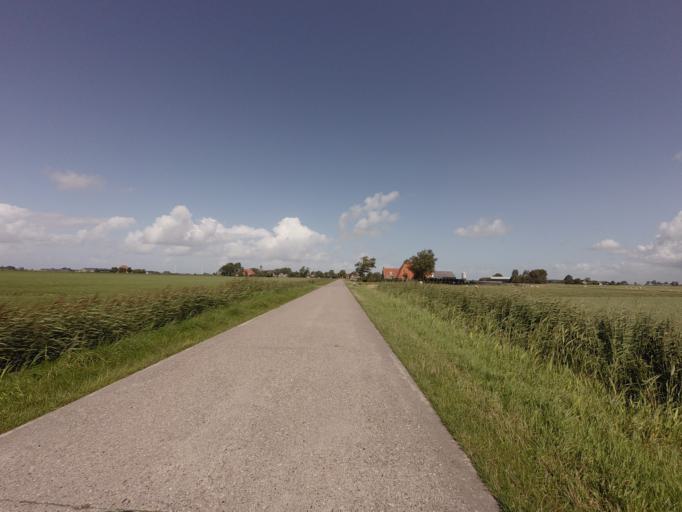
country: NL
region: Friesland
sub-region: Sudwest Fryslan
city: Makkum
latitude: 53.0748
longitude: 5.4532
